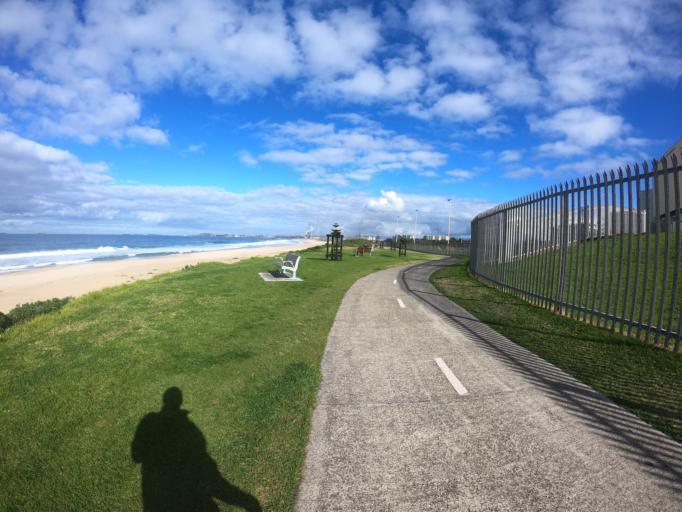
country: AU
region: New South Wales
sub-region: Wollongong
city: Wollongong
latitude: -34.4286
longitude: 150.9034
